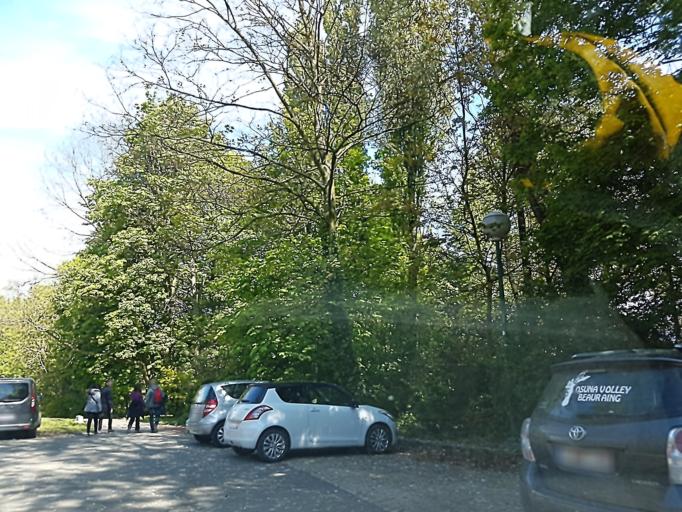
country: BE
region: Brussels Capital
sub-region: Bruxelles-Capitale
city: Brussels
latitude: 50.8917
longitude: 4.3528
